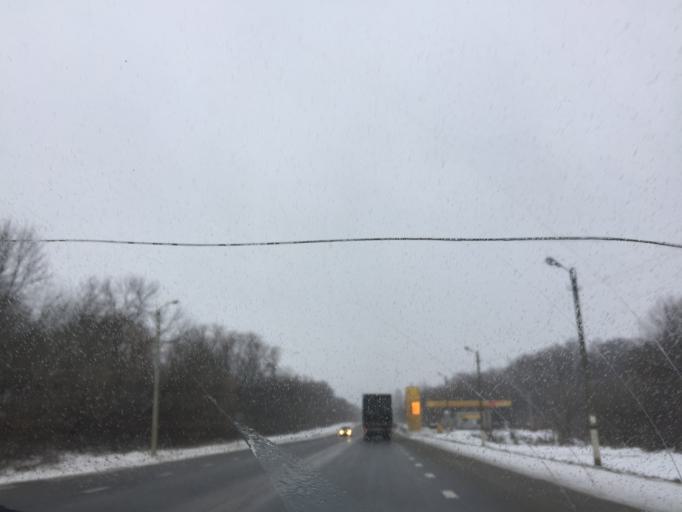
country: RU
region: Tula
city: Plavsk
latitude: 53.7458
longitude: 37.3227
